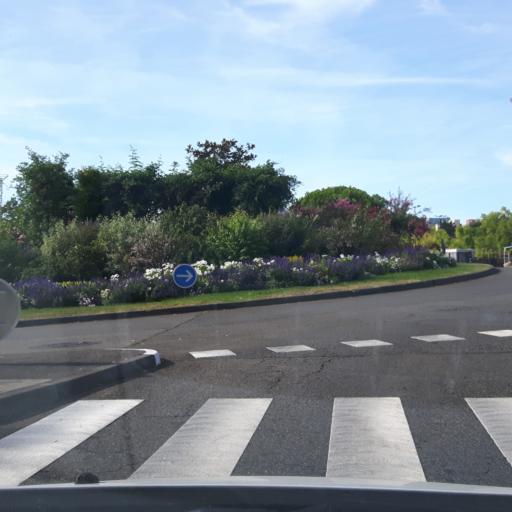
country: FR
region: Midi-Pyrenees
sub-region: Departement de la Haute-Garonne
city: Balma
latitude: 43.5878
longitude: 1.4912
